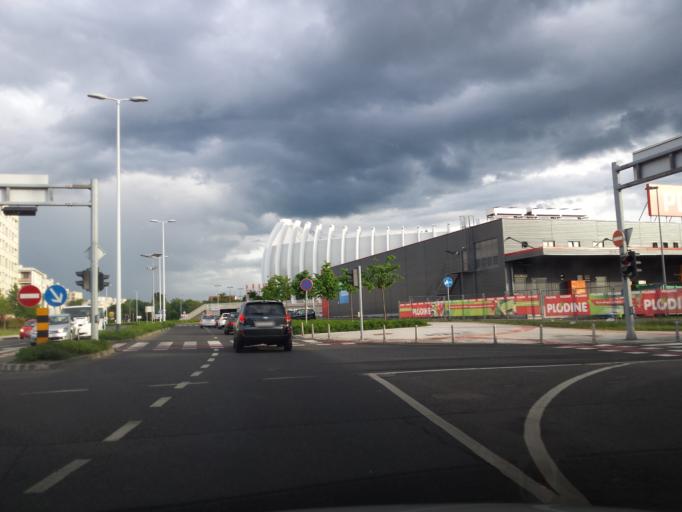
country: HR
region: Grad Zagreb
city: Novi Zagreb
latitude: 45.7738
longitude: 15.9432
